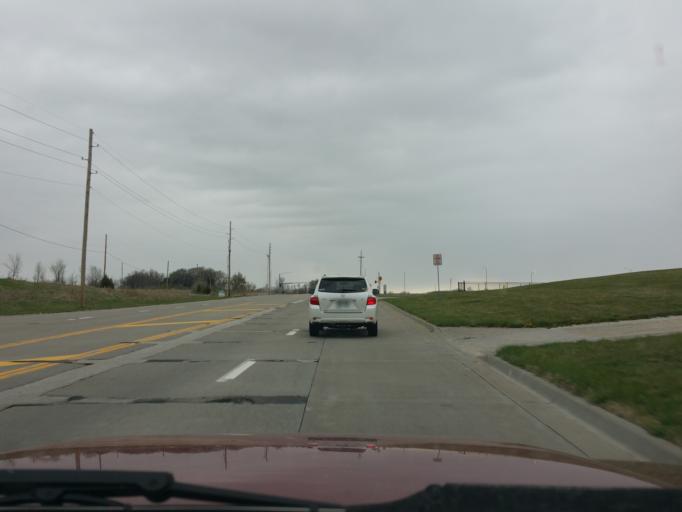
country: US
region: Kansas
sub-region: Wyandotte County
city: Bonner Springs
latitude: 39.1133
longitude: -94.8537
